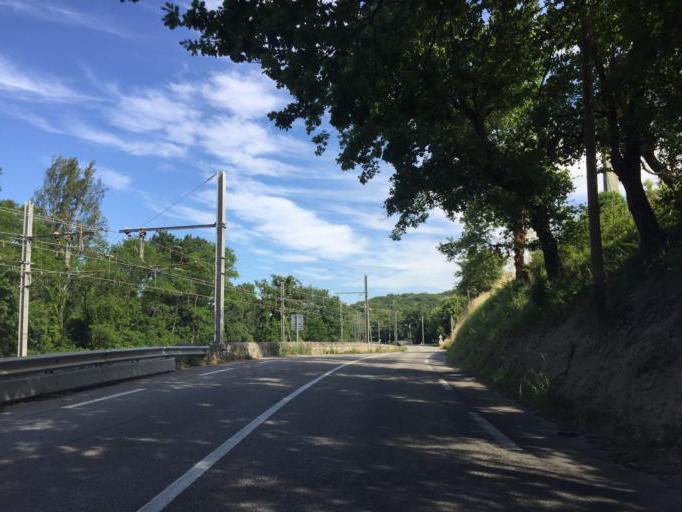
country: FR
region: Rhone-Alpes
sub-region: Departement de l'Ardeche
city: Le Pouzin
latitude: 44.7226
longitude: 4.7473
